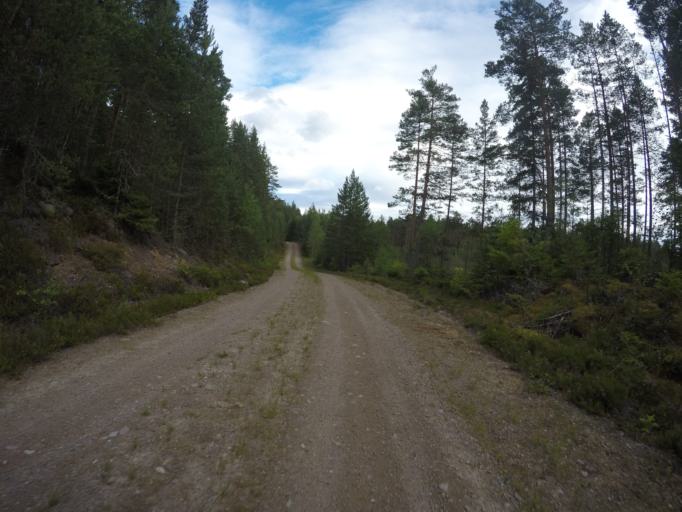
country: SE
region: Vaermland
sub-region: Filipstads Kommun
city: Lesjofors
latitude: 60.0292
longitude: 14.3820
